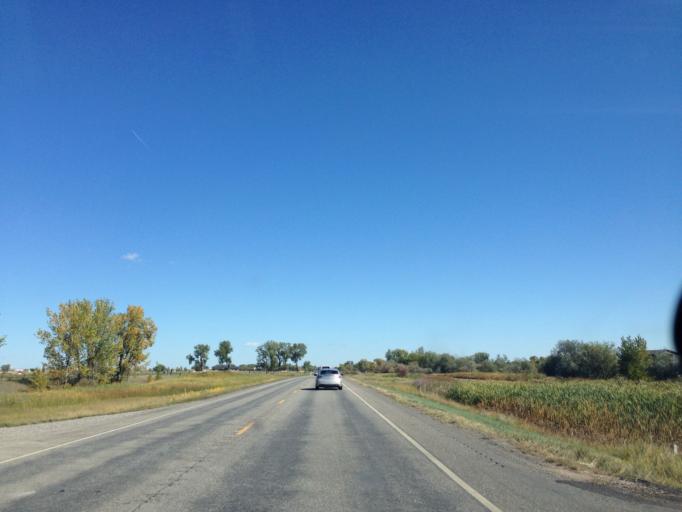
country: US
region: Montana
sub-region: Yellowstone County
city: Laurel
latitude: 45.5993
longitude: -108.8075
